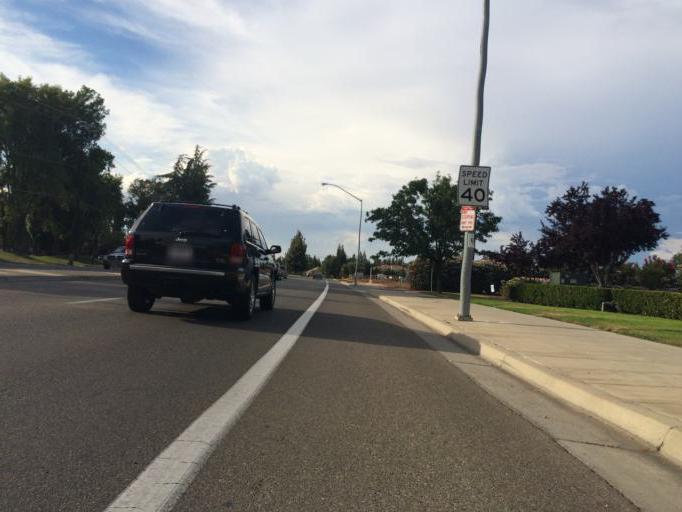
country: US
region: California
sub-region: Fresno County
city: Clovis
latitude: 36.8524
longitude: -119.7745
